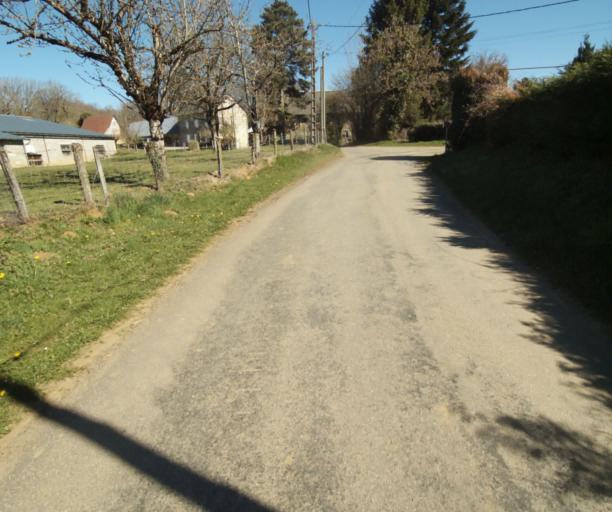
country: FR
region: Limousin
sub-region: Departement de la Correze
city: Seilhac
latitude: 45.3498
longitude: 1.7288
